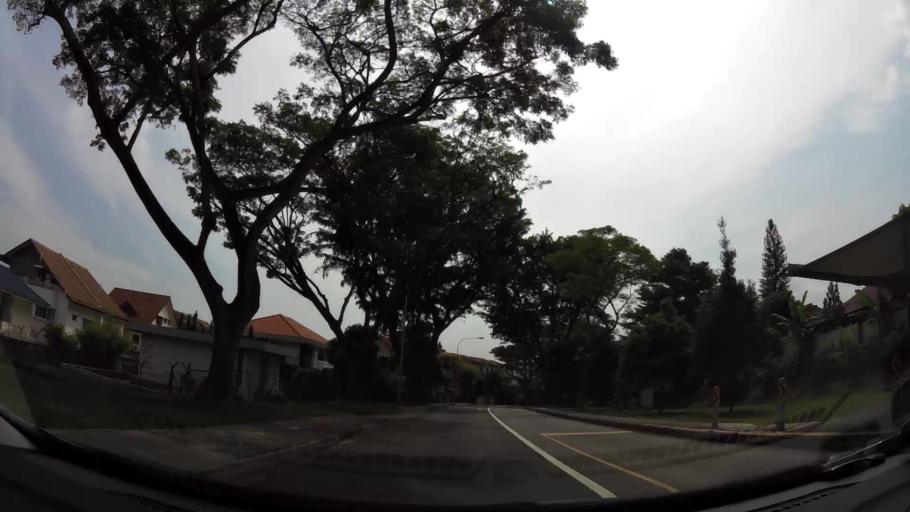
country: SG
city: Singapore
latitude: 1.3635
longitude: 103.9700
